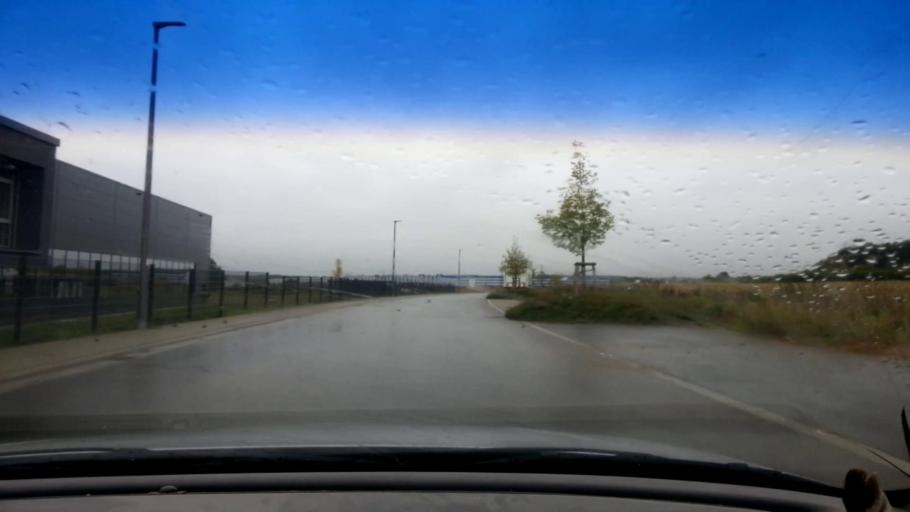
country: DE
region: Bavaria
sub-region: Upper Franconia
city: Schesslitz
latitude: 49.9784
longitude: 11.0561
